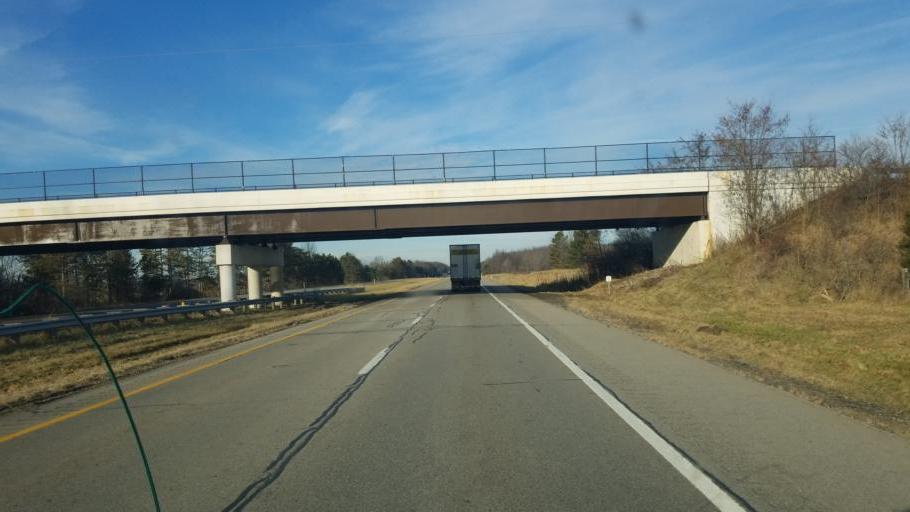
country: US
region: Ohio
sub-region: Ashtabula County
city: Orwell
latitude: 41.5059
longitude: -80.7132
